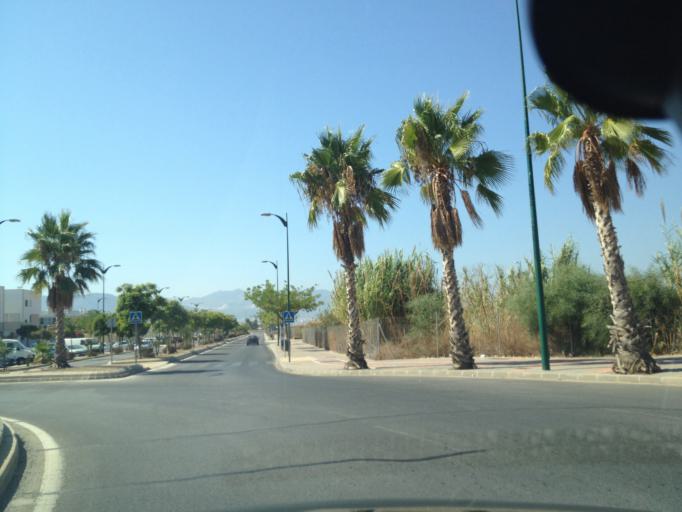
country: ES
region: Andalusia
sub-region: Provincia de Malaga
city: Malaga
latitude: 36.7237
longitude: -4.4929
